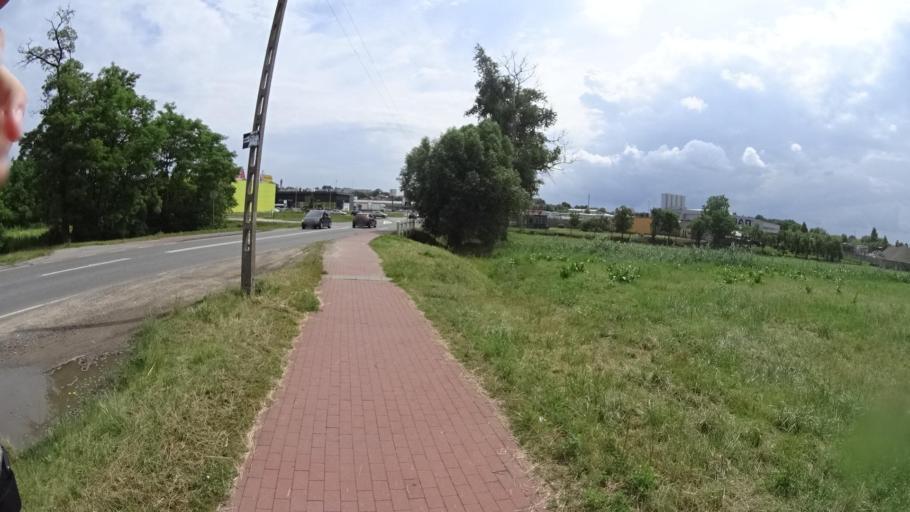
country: PL
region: Masovian Voivodeship
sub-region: Powiat grojecki
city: Grojec
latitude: 51.8751
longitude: 20.8642
